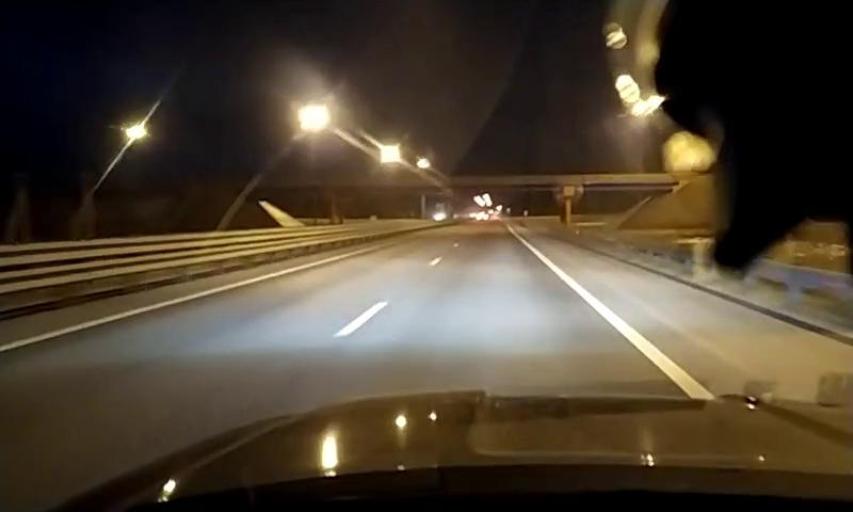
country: RU
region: Leningrad
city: Agalatovo
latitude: 60.2230
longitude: 30.3585
